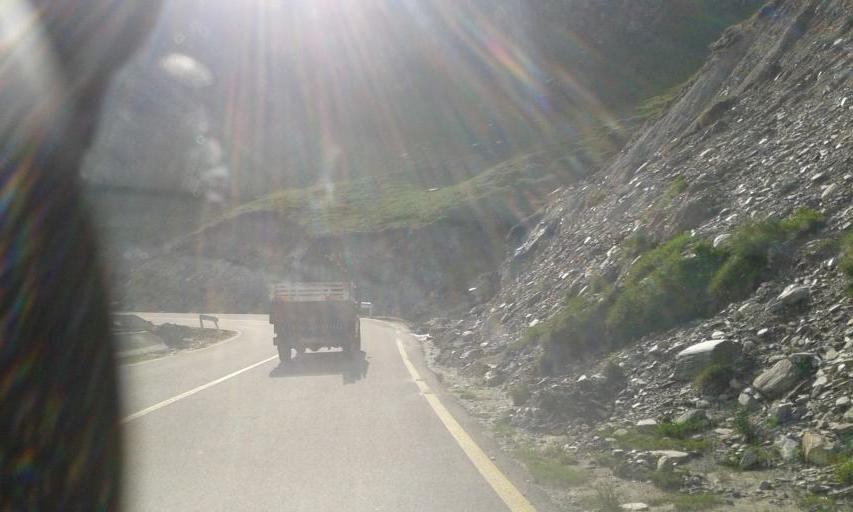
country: RO
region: Gorj
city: Novaci-Straini
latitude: 45.3579
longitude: 23.6539
